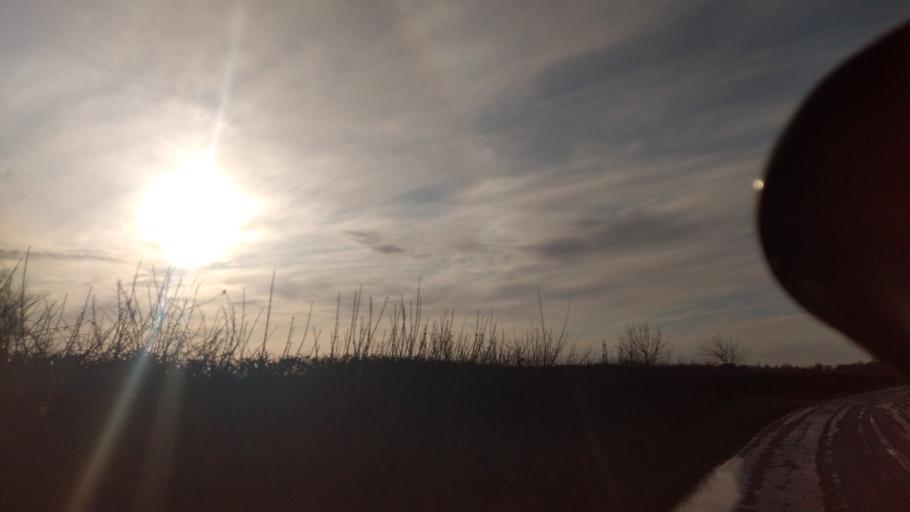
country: GB
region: England
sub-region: Wiltshire
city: Corsham
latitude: 51.4573
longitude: -2.1639
